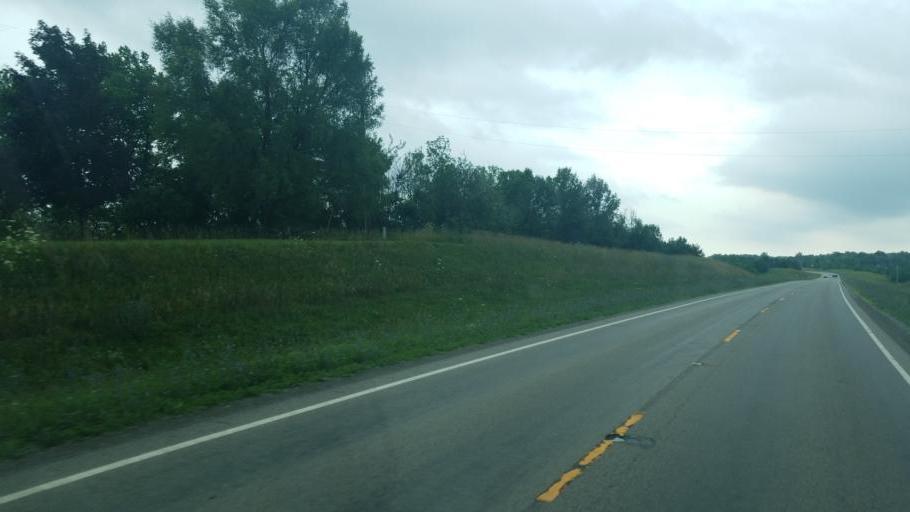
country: US
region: Ohio
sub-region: Logan County
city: Russells Point
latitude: 40.5835
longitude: -83.8396
